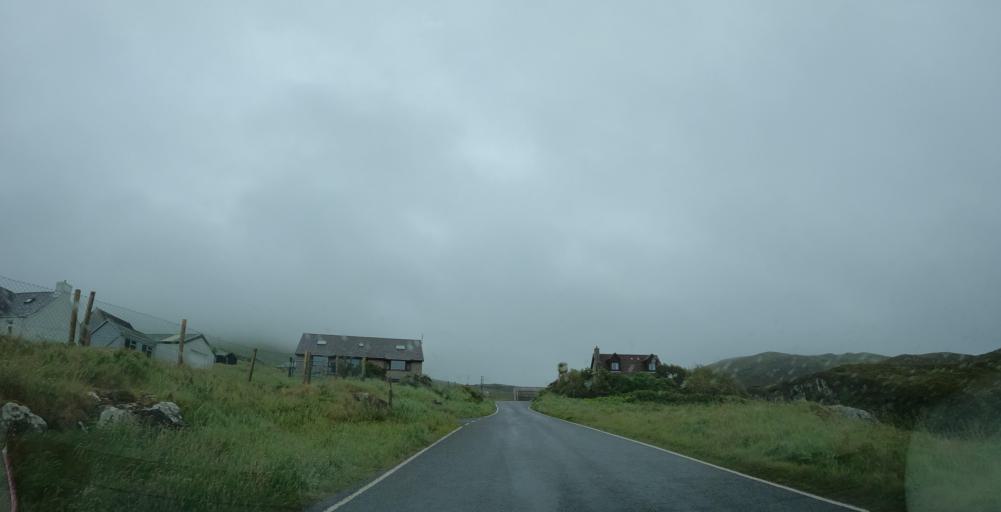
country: GB
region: Scotland
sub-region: Eilean Siar
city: Barra
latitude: 56.9561
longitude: -7.4729
